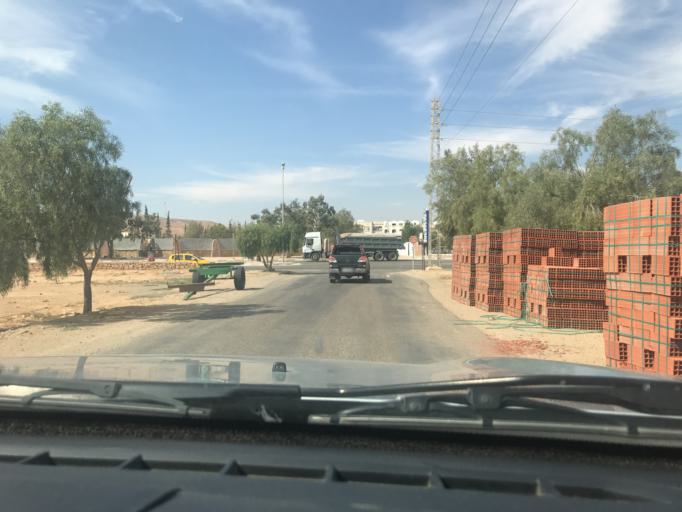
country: TN
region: Tataouine
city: Tataouine
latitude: 32.9913
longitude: 10.4629
